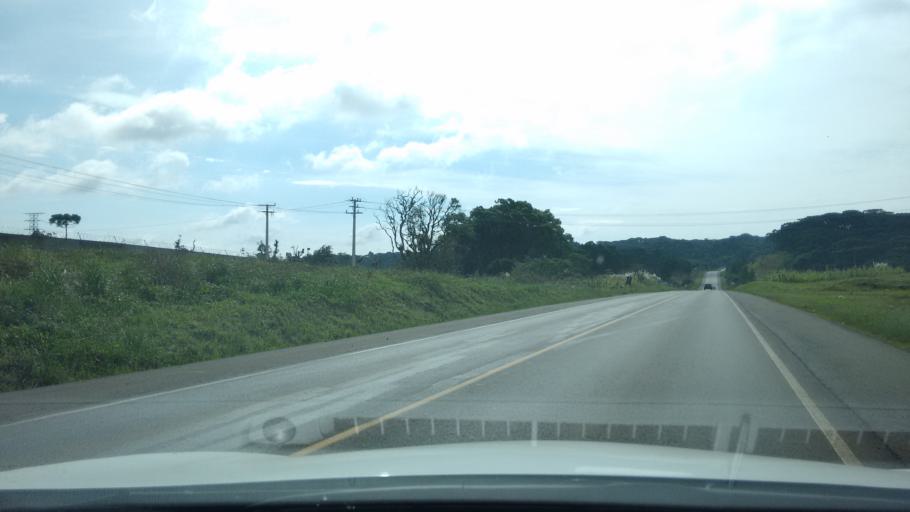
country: BR
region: Santa Catarina
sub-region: Curitibanos
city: Curitibanos
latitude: -27.3153
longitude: -50.5396
